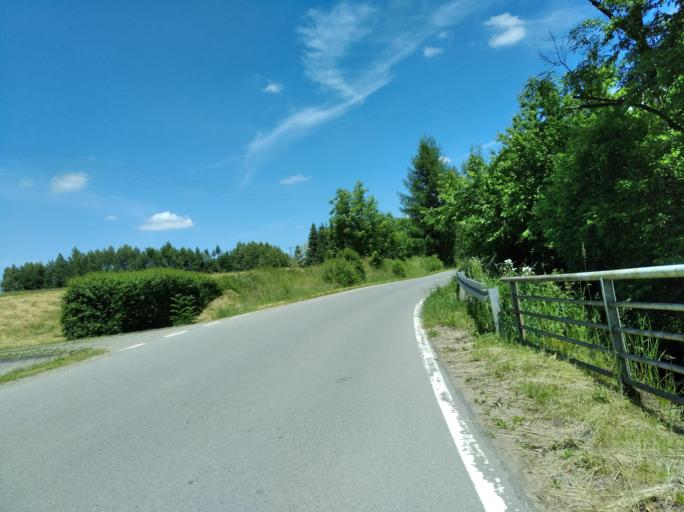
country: PL
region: Subcarpathian Voivodeship
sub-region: Powiat krosnienski
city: Wojaszowka
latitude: 49.7848
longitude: 21.6840
